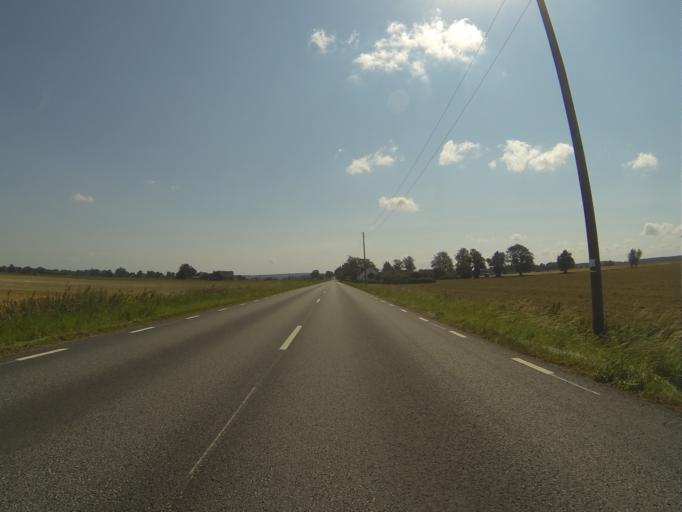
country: SE
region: Skane
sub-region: Eslovs Kommun
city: Eslov
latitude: 55.7505
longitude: 13.3236
